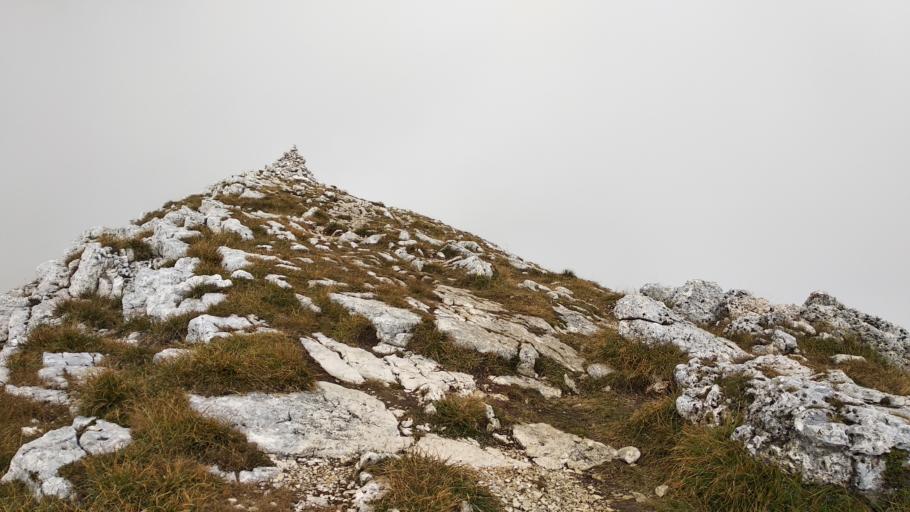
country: IT
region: Trentino-Alto Adige
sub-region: Provincia di Trento
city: Borgo
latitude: 45.9782
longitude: 11.4471
